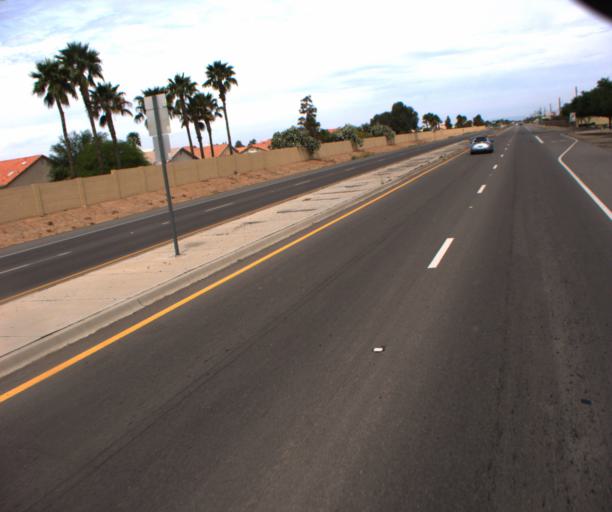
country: US
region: Arizona
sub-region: Maricopa County
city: Sun Lakes
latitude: 33.2066
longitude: -111.8411
